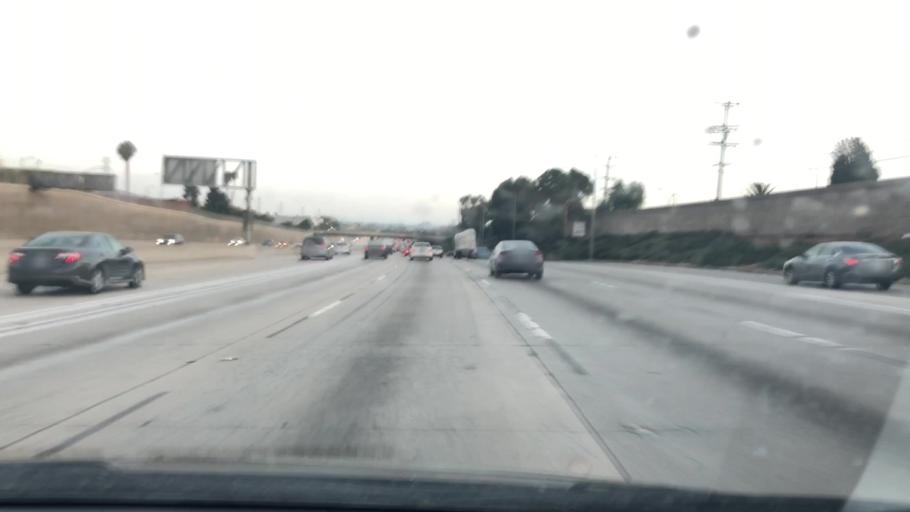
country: US
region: California
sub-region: Los Angeles County
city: West Athens
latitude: 33.9137
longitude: -118.2868
